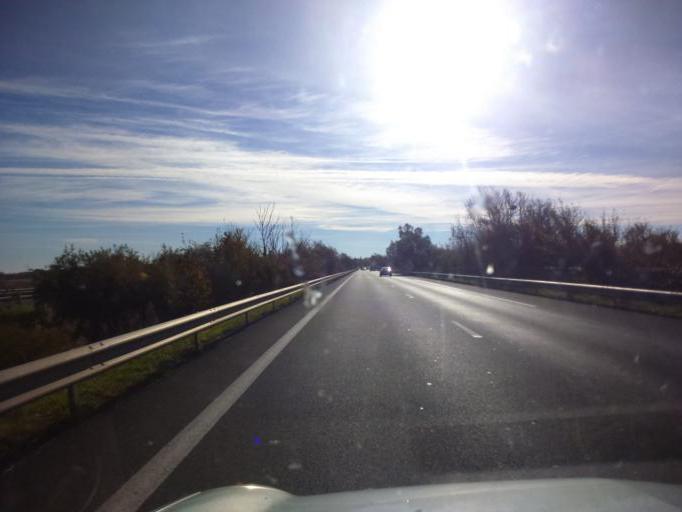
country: FR
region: Poitou-Charentes
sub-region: Departement de la Charente-Maritime
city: Breuil-Magne
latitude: 45.9764
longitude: -0.9934
